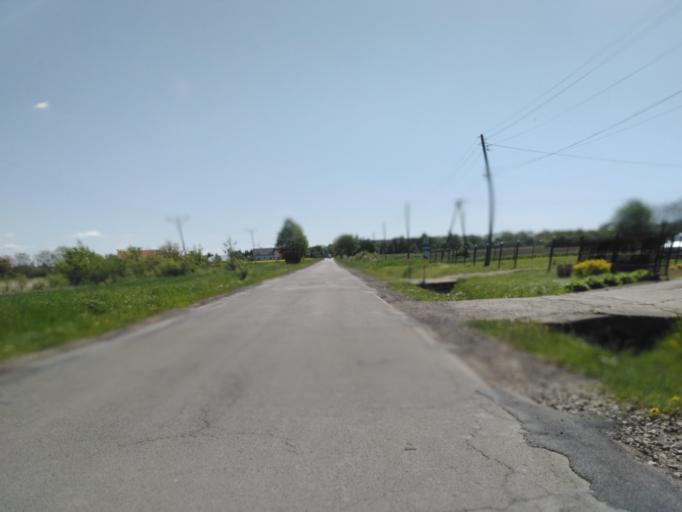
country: PL
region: Subcarpathian Voivodeship
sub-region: Powiat krosnienski
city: Miejsce Piastowe
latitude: 49.6061
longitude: 21.7834
